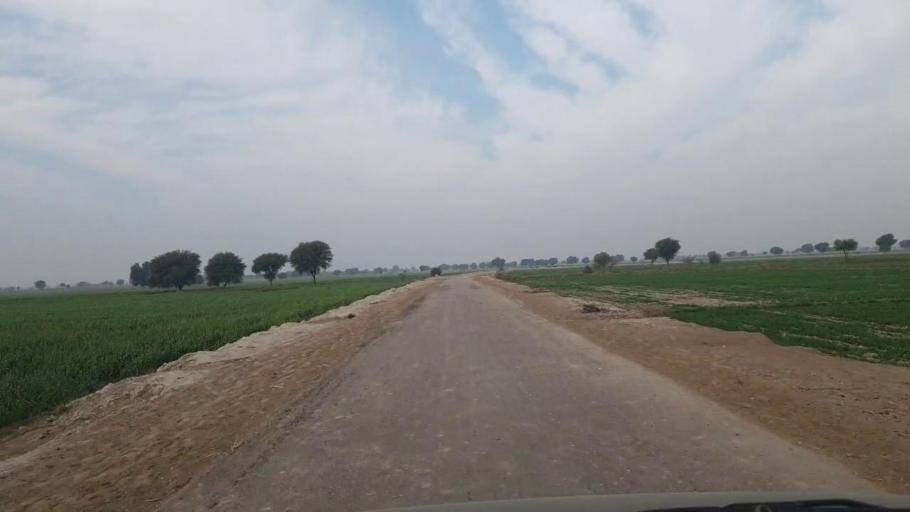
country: PK
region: Sindh
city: Shahdadpur
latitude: 25.9506
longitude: 68.6733
